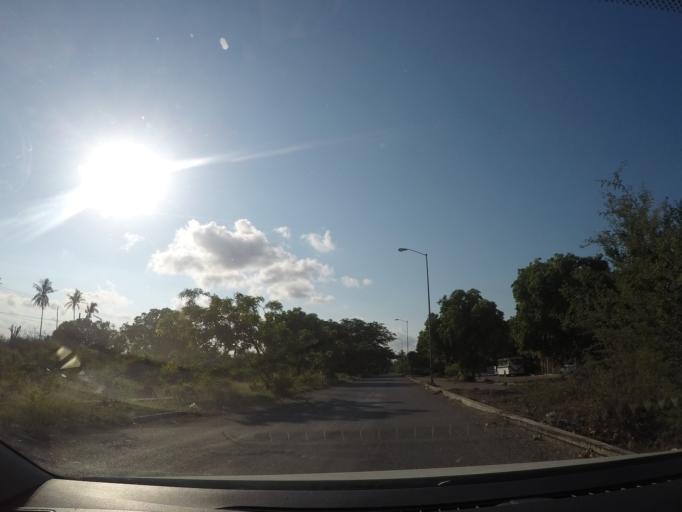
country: MX
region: Oaxaca
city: Juchitan de Zaragoza
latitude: 16.4239
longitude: -95.0295
